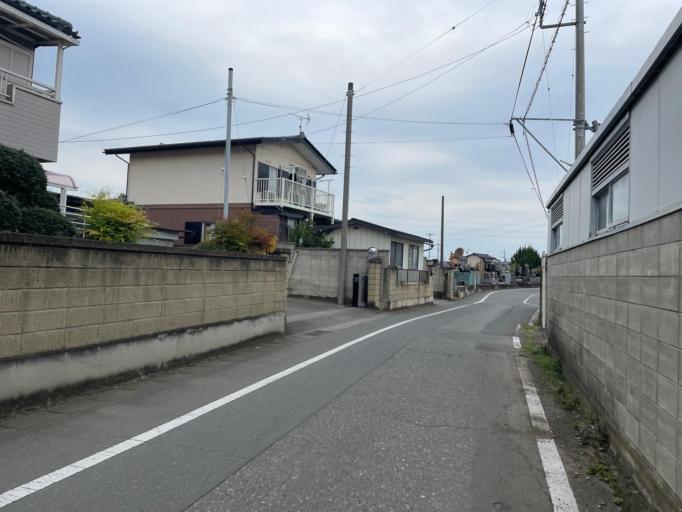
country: JP
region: Gunma
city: Sakai-nakajima
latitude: 36.2749
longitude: 139.2464
